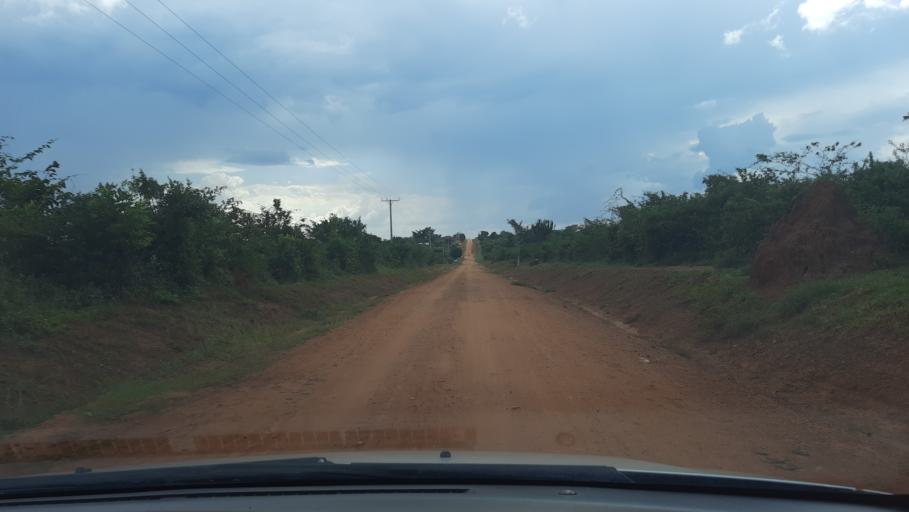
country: UG
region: Central Region
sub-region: Nakasongola District
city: Nakasongola
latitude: 1.3807
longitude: 32.5076
